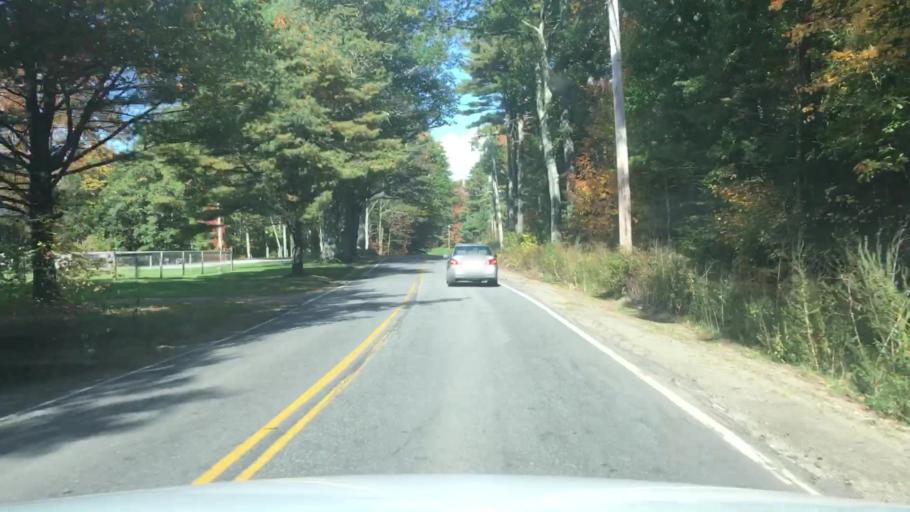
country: US
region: Maine
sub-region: Knox County
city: Warren
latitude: 44.1416
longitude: -69.2349
